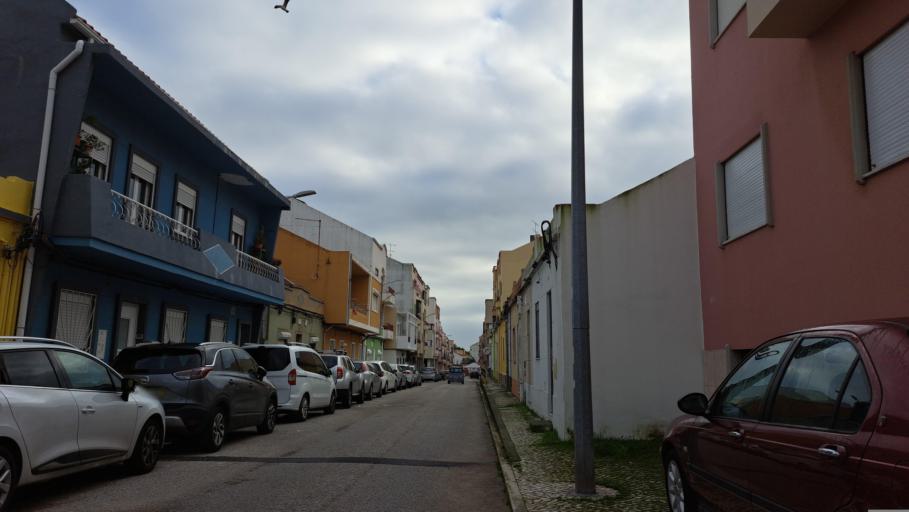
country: PT
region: Setubal
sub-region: Barreiro
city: Barreiro
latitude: 38.6582
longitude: -9.0491
